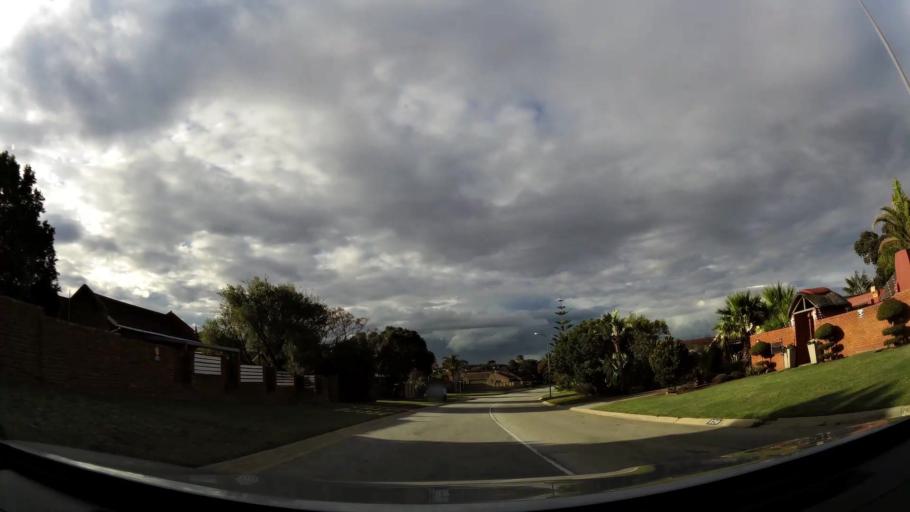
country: ZA
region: Eastern Cape
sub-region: Nelson Mandela Bay Metropolitan Municipality
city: Port Elizabeth
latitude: -33.9547
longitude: 25.4810
